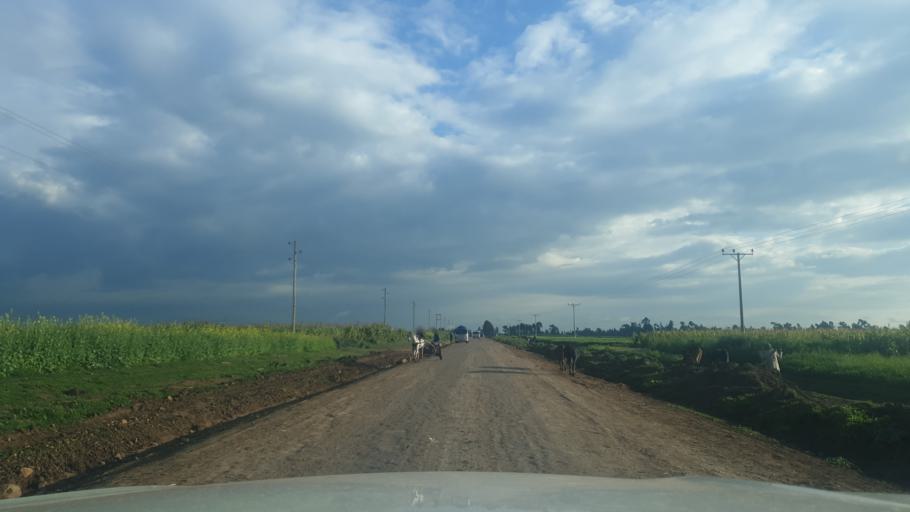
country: ET
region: Oromiya
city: Ziway
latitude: 7.7453
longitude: 39.0359
